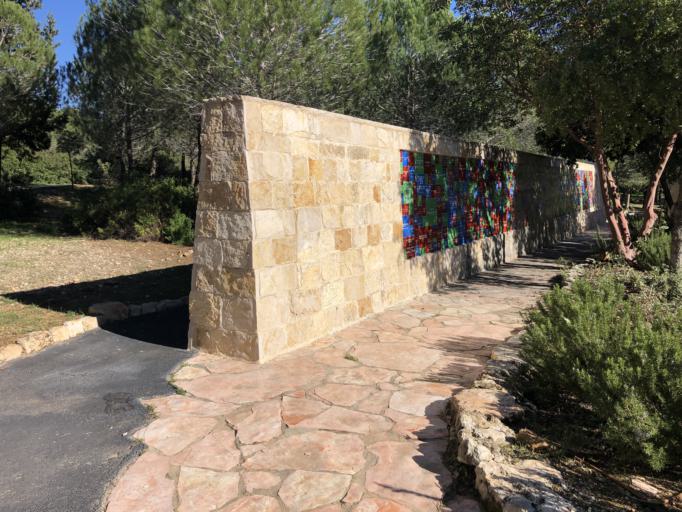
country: IL
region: Jerusalem
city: Zur Hadassa
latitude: 31.7476
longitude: 35.0472
